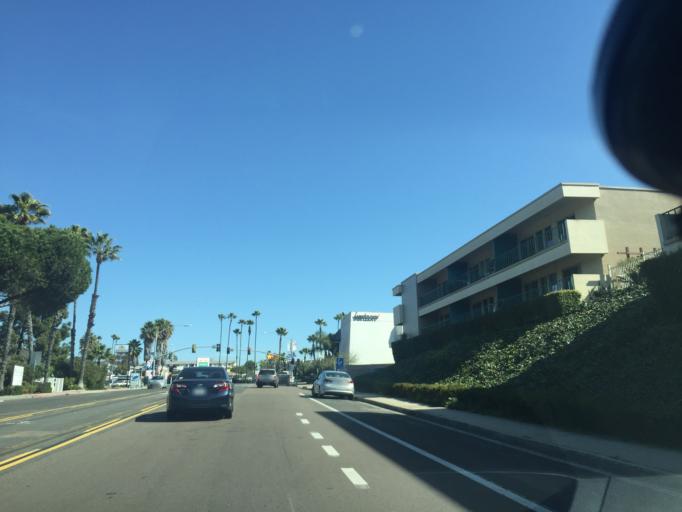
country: US
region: California
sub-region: San Diego County
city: San Diego
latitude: 32.7938
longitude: -117.1952
